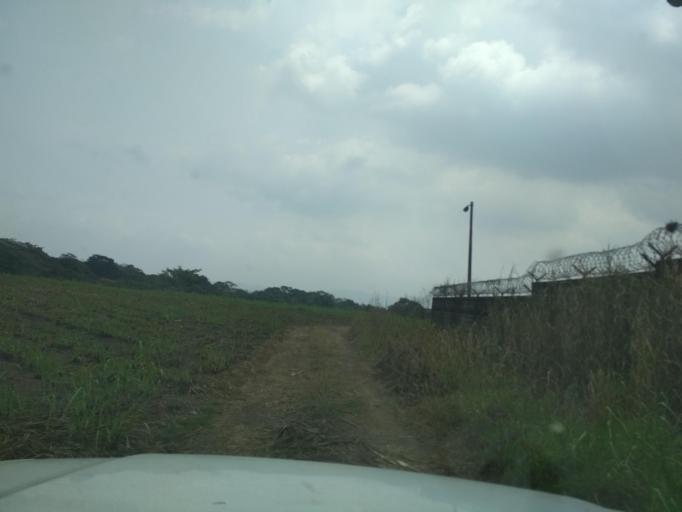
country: MX
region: Veracruz
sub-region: Cordoba
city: San Jose de Tapia
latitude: 18.8361
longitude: -96.9746
